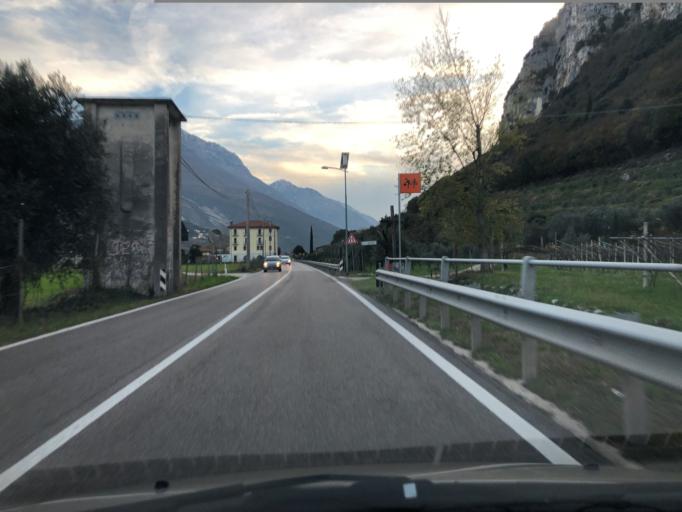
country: IT
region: Trentino-Alto Adige
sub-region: Provincia di Trento
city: Nago-Torbole
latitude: 45.8892
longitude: 10.8791
